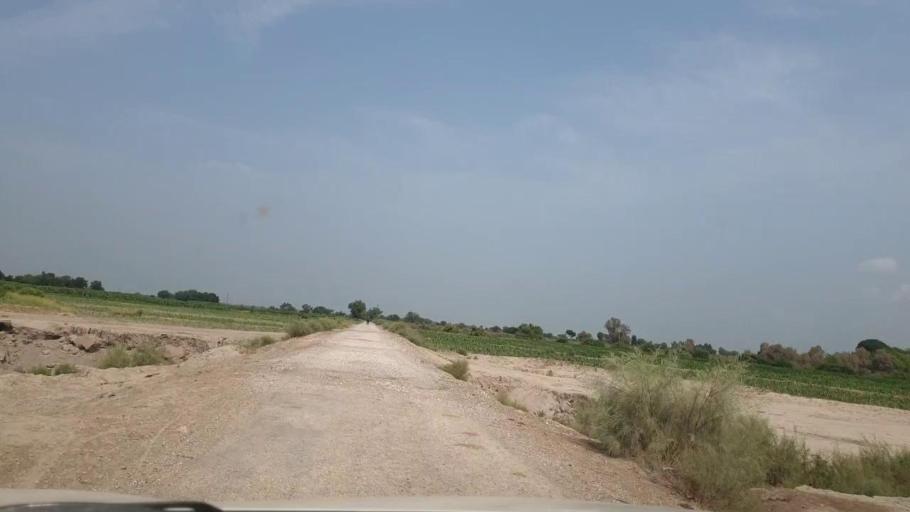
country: PK
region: Sindh
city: Sobhadero
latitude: 27.3883
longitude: 68.2732
